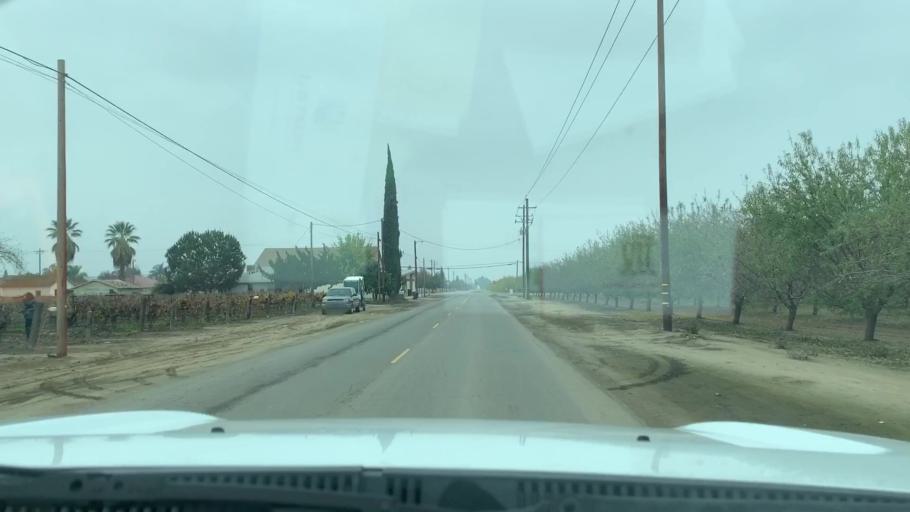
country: US
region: California
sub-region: Kern County
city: Shafter
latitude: 35.5015
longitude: -119.2961
